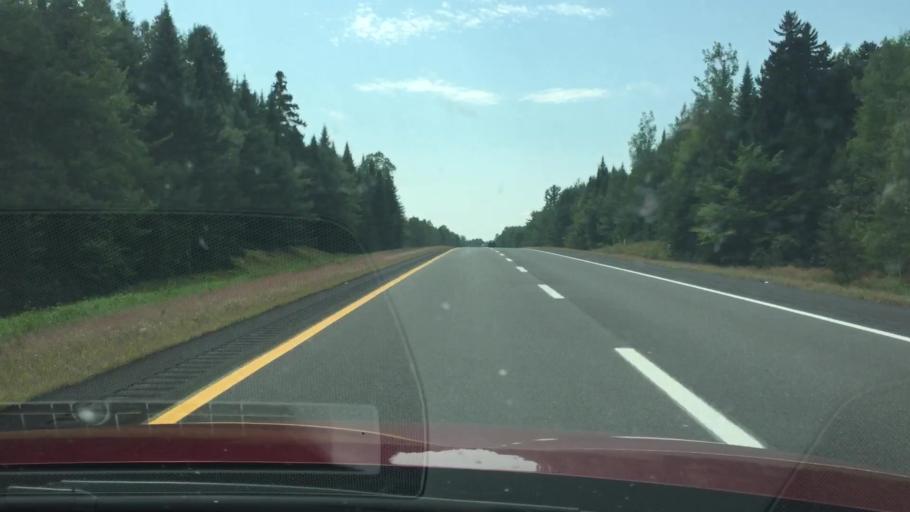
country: US
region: Maine
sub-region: Penobscot County
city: Patten
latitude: 46.0620
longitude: -68.2327
